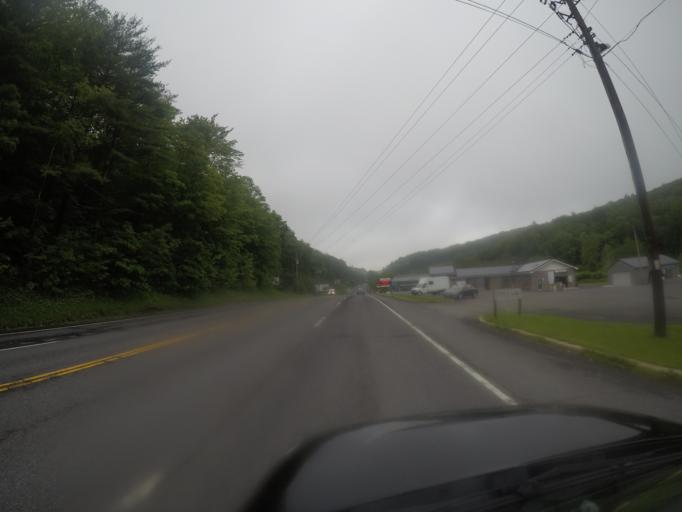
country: US
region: New York
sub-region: Ulster County
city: Hurley
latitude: 41.9632
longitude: -74.0617
